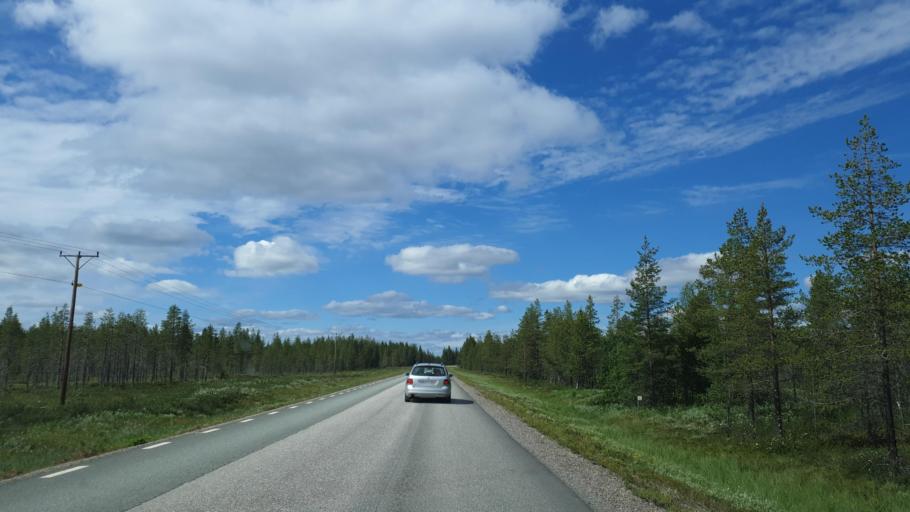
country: SE
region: Norrbotten
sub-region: Arjeplogs Kommun
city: Arjeplog
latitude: 65.5692
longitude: 18.2378
